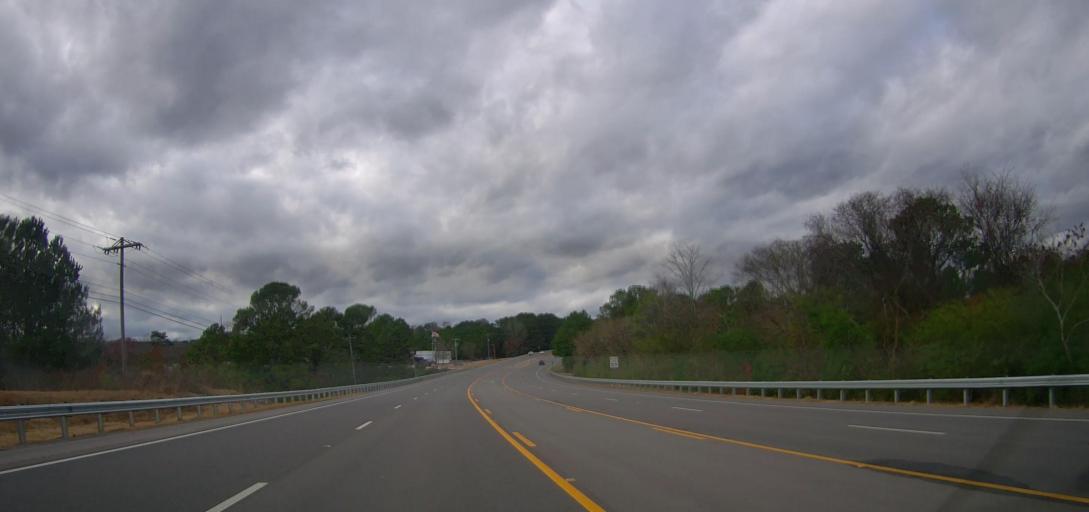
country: US
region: Alabama
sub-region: Cullman County
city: Cullman
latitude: 34.2086
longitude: -86.8845
